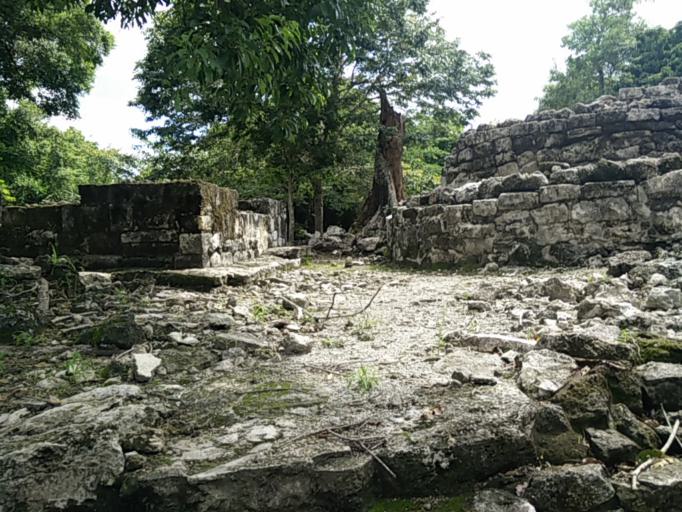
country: MX
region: Quintana Roo
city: San Miguel de Cozumel
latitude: 20.5038
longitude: -86.8463
